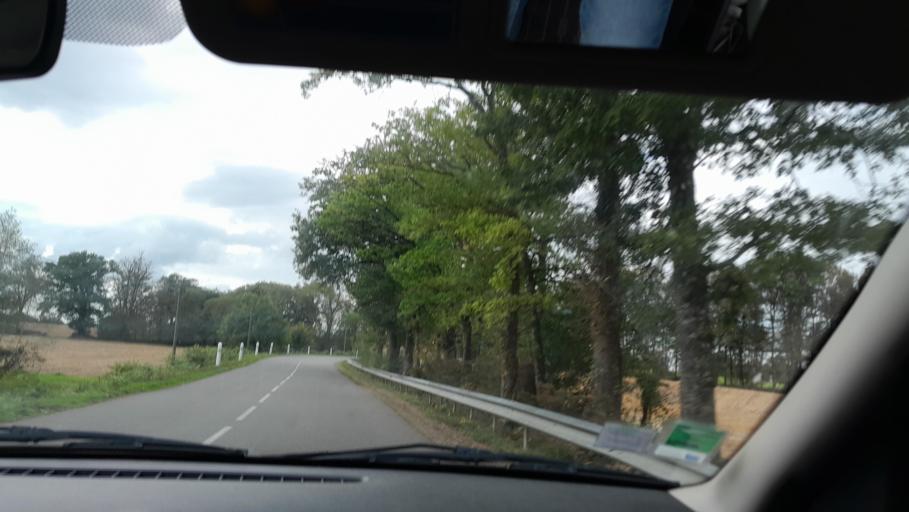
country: FR
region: Brittany
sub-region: Departement d'Ille-et-Vilaine
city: Le Pertre
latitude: 48.0468
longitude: -1.0883
